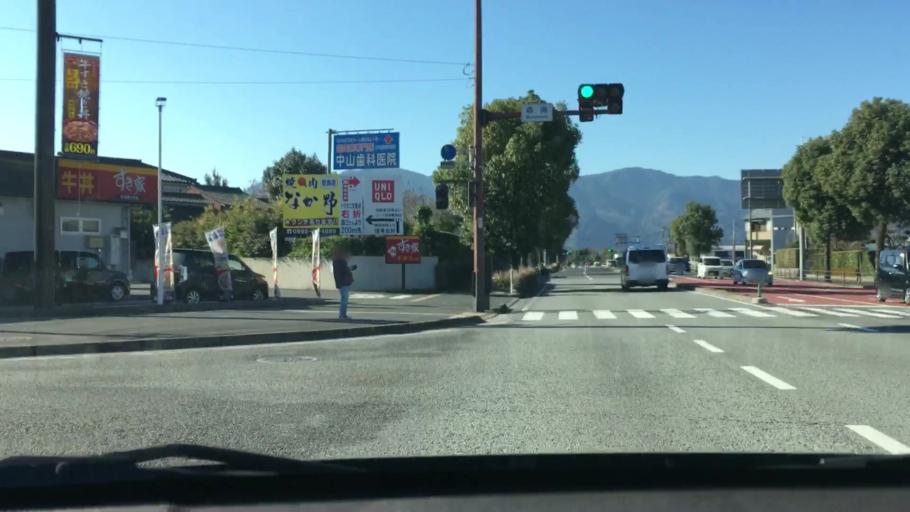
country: JP
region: Kagoshima
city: Kajiki
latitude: 31.7310
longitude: 130.6286
